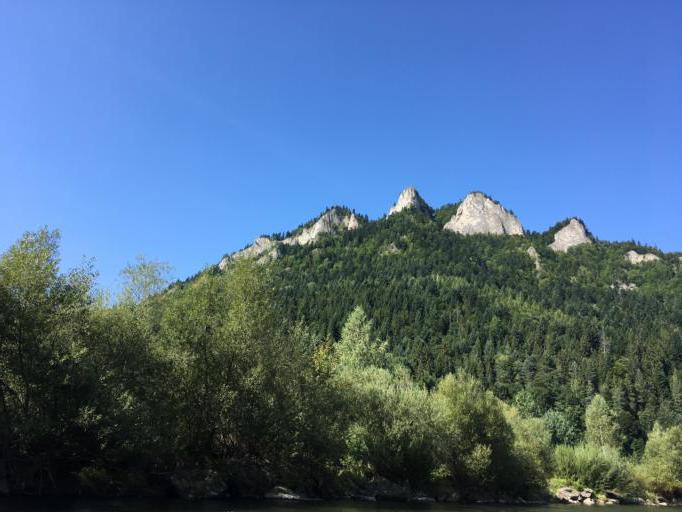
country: PL
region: Lesser Poland Voivodeship
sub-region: Powiat nowotarski
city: Kroscienko nad Dunajcem
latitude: 49.4043
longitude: 20.4146
